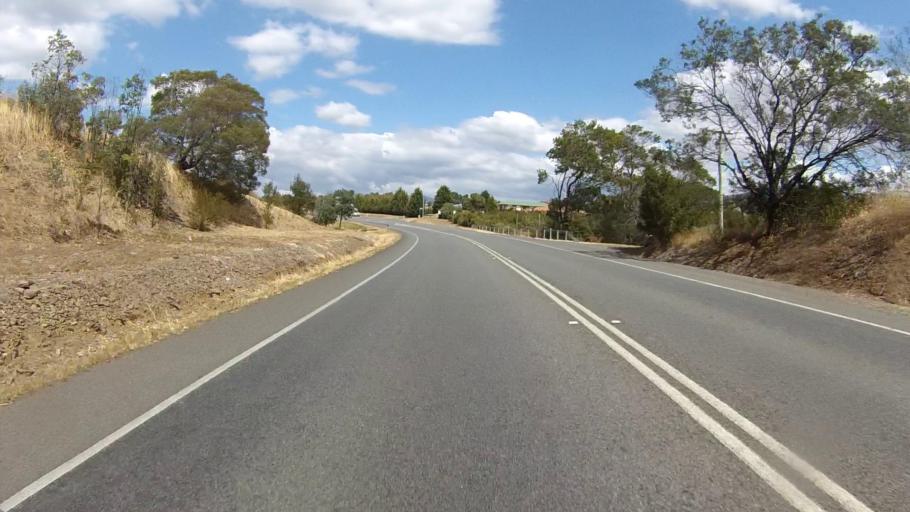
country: AU
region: Tasmania
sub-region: Glenorchy
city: Austins Ferry
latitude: -42.7566
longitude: 147.2683
